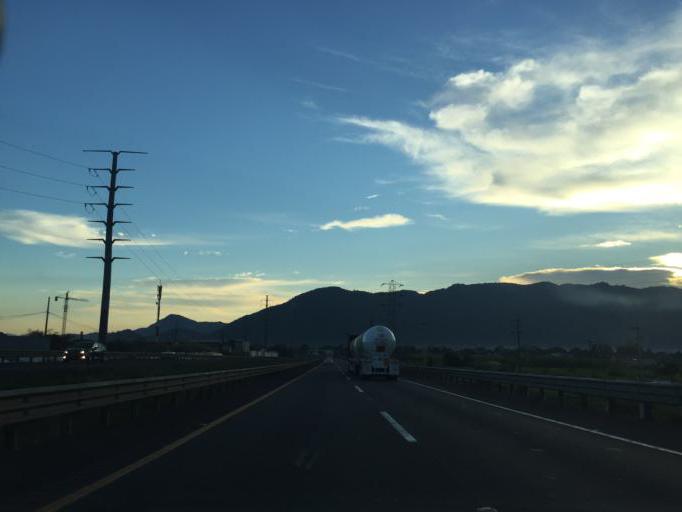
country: MX
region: Veracruz
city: Jalapilla
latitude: 18.8308
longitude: -97.0997
